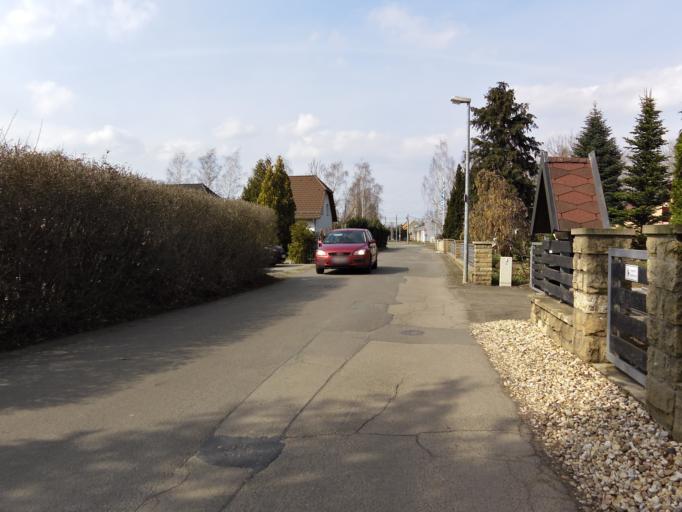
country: DE
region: Saxony
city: Markranstadt
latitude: 51.3102
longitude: 12.2800
